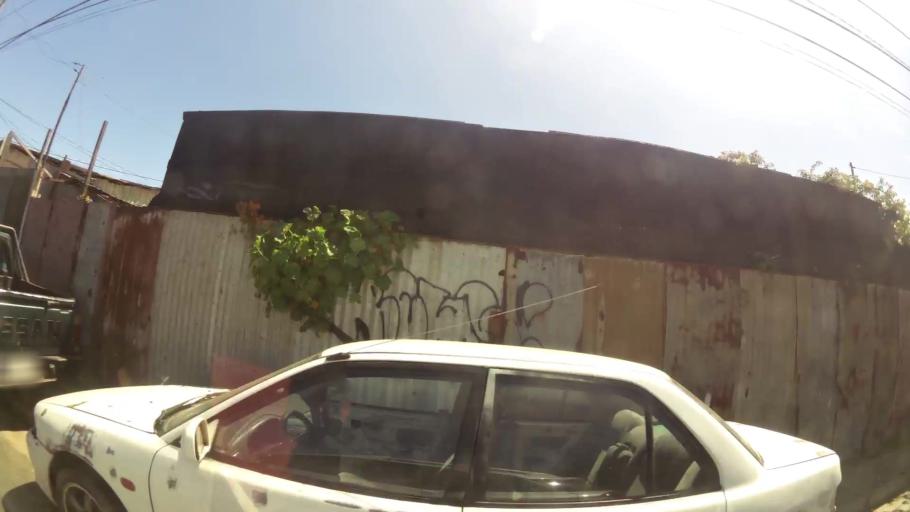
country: CL
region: Valparaiso
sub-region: Provincia de Valparaiso
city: Valparaiso
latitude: -33.0352
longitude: -71.6519
